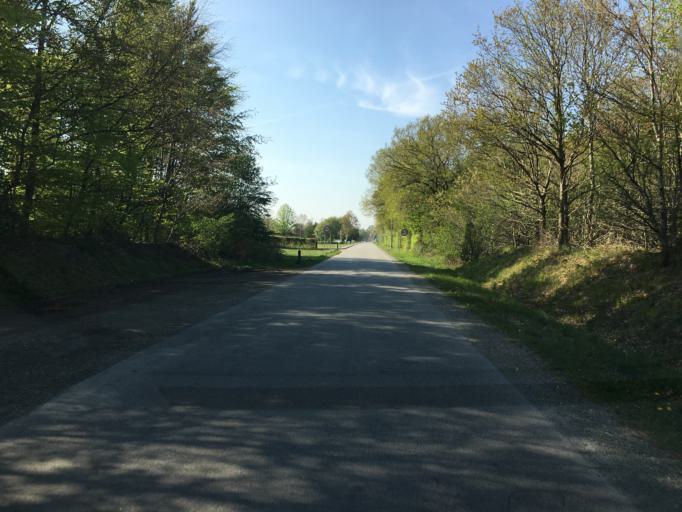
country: DK
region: South Denmark
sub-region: Haderslev Kommune
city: Vojens
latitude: 55.2432
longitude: 9.3186
